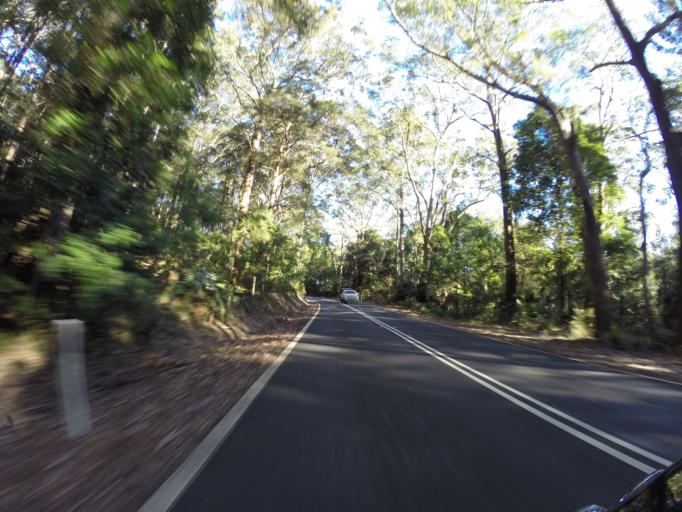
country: AU
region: New South Wales
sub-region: Wollongong
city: Helensburgh
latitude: -34.1905
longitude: 151.0108
